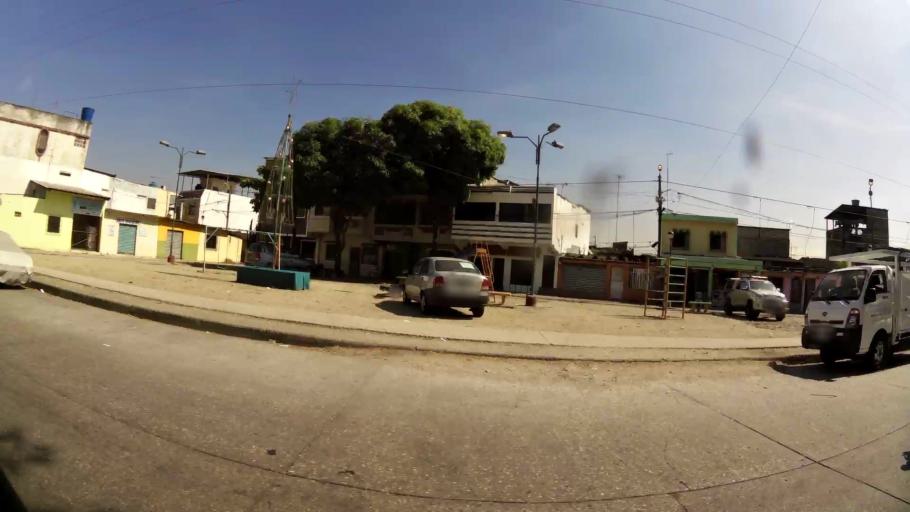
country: EC
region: Guayas
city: Eloy Alfaro
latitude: -2.1257
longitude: -79.8914
